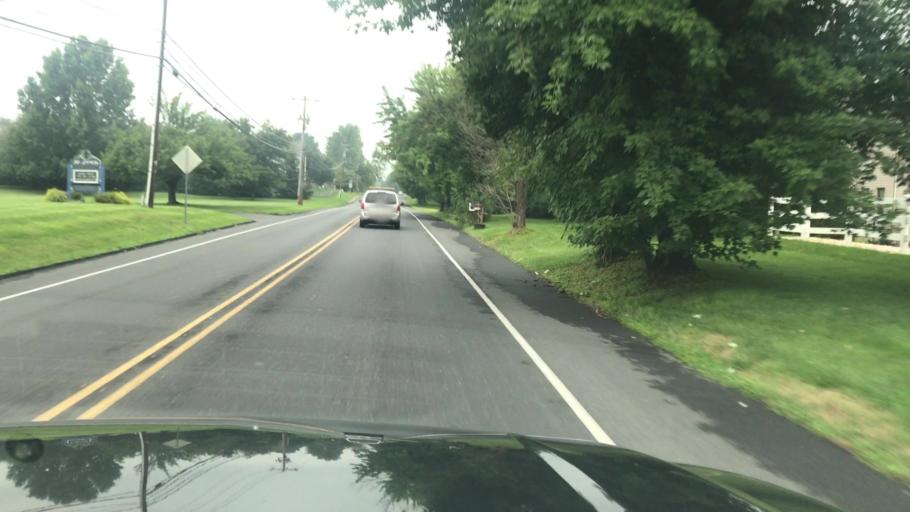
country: US
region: Pennsylvania
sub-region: Cumberland County
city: Enola
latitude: 40.2755
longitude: -76.9703
